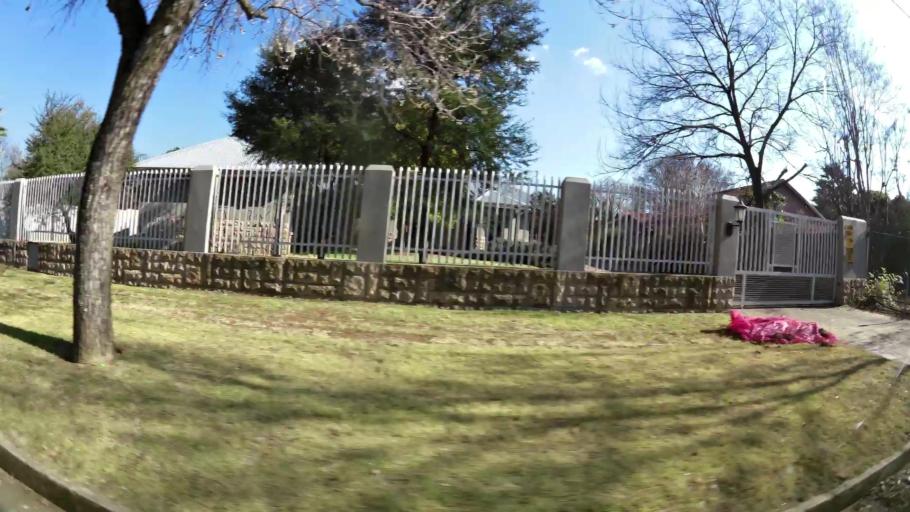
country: ZA
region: Gauteng
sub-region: Ekurhuleni Metropolitan Municipality
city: Benoni
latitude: -26.1466
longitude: 28.3348
